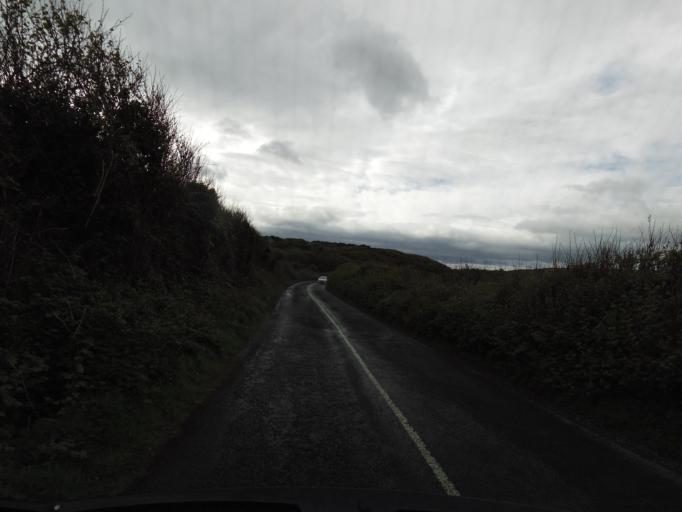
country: IE
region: Connaught
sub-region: County Galway
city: Bearna
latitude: 53.0557
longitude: -9.3526
